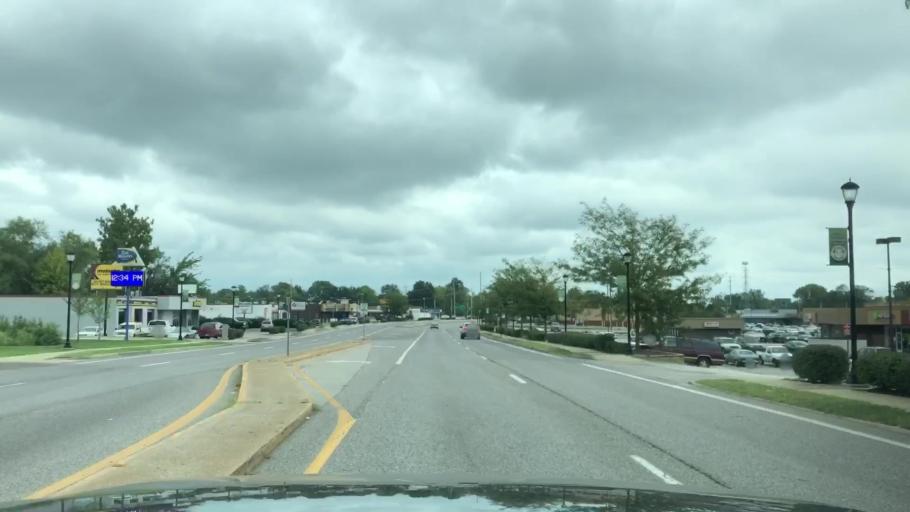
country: US
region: Missouri
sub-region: Saint Louis County
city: Florissant
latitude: 38.7975
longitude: -90.3381
